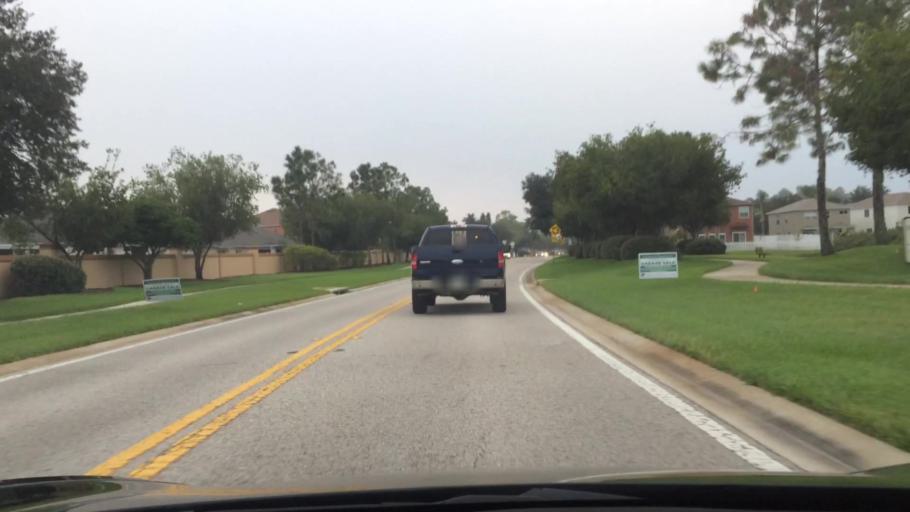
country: US
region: Florida
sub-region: Hillsborough County
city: Pebble Creek
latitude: 28.1807
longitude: -82.3660
